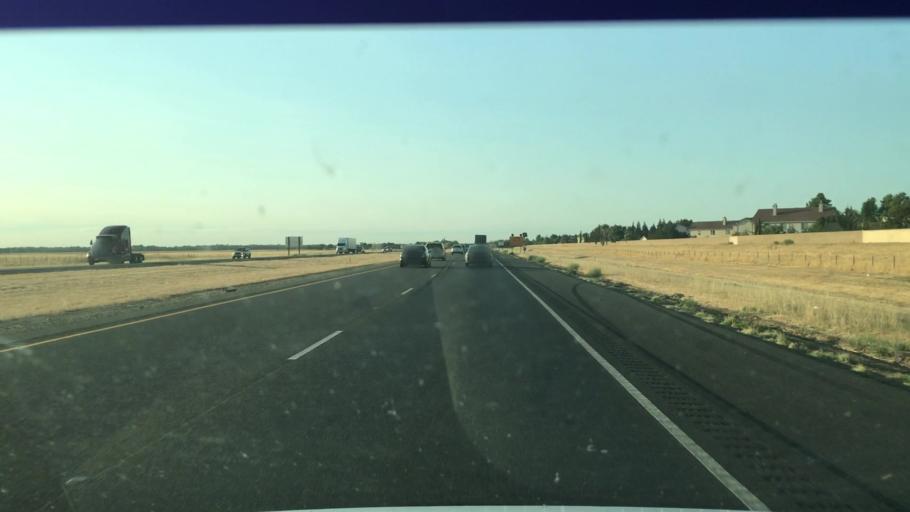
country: US
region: California
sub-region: Sacramento County
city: Laguna
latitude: 38.3946
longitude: -121.4806
